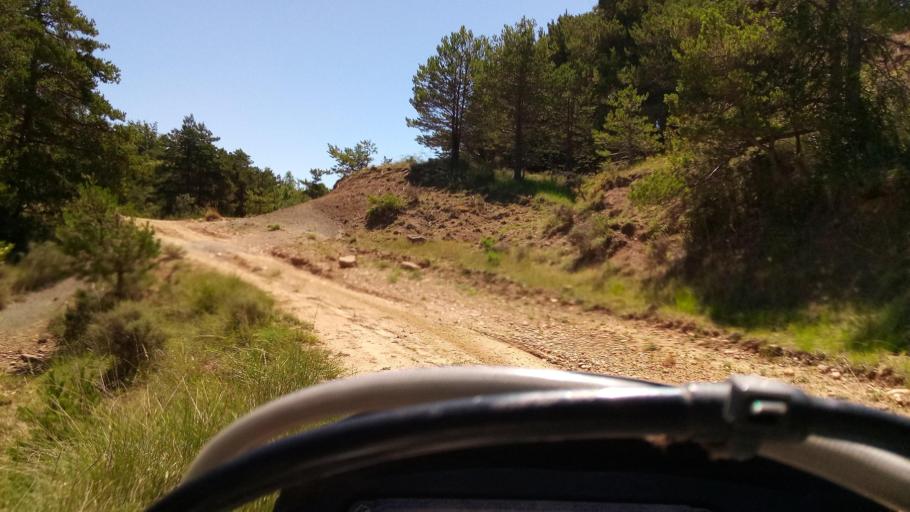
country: ES
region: Aragon
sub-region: Provincia de Huesca
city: Lascuarre
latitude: 42.3050
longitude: 0.4933
